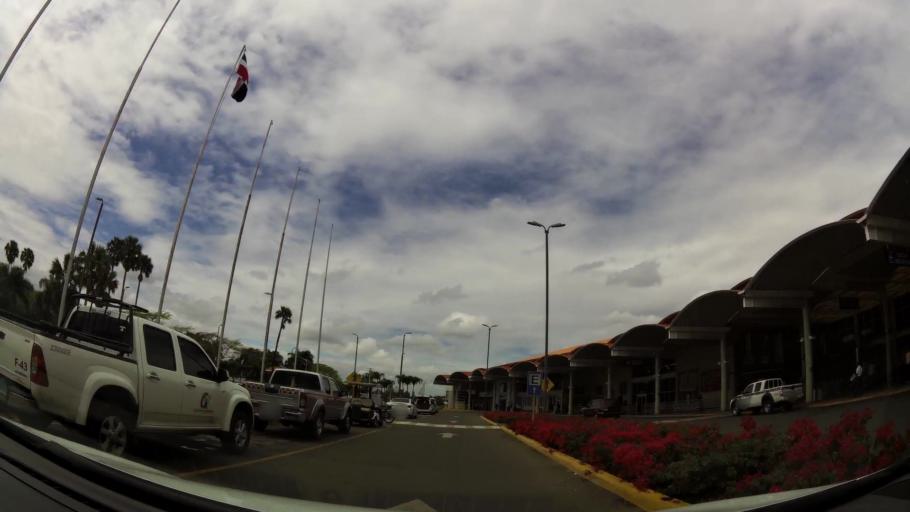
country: DO
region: Santiago
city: Licey al Medio
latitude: 19.4019
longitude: -70.6018
